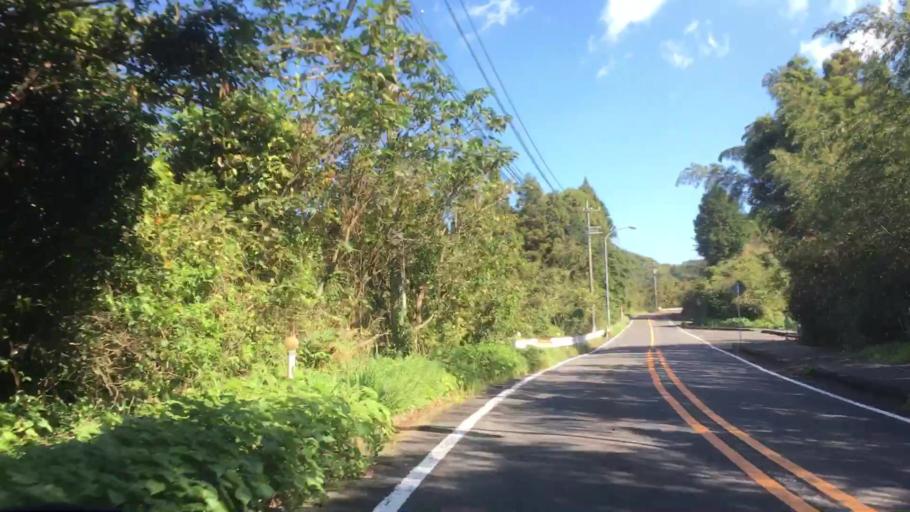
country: JP
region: Nagasaki
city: Sasebo
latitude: 33.0292
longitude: 129.6546
